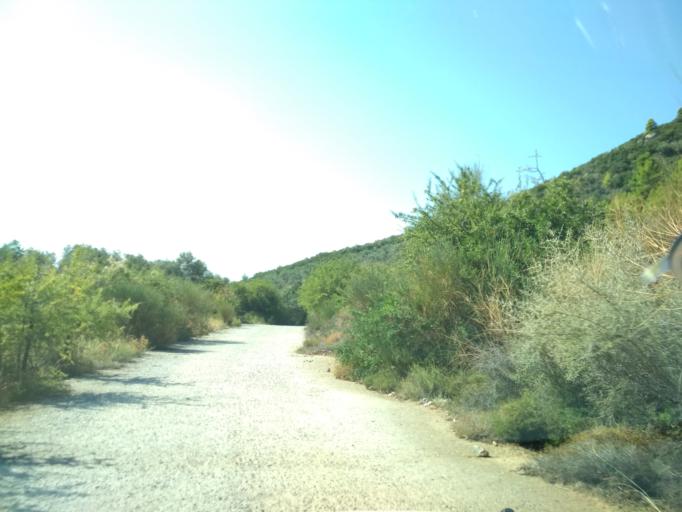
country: GR
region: Central Greece
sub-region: Nomos Evvoias
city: Oreoi
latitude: 38.8522
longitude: 23.1196
